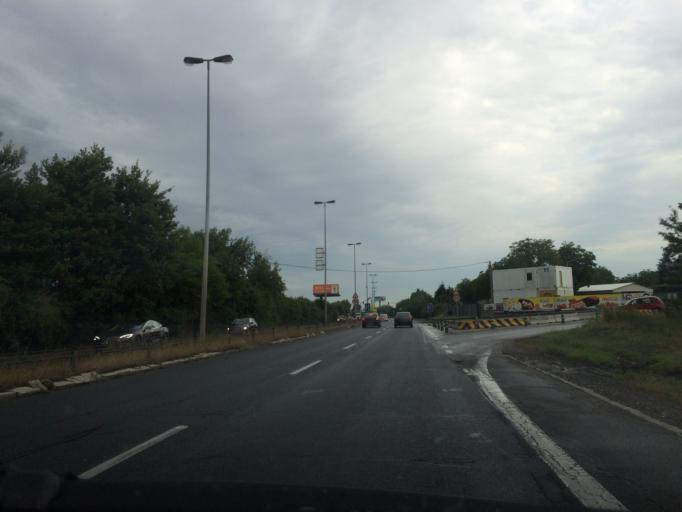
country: CZ
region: Central Bohemia
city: Tuchomerice
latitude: 50.1013
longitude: 14.2952
